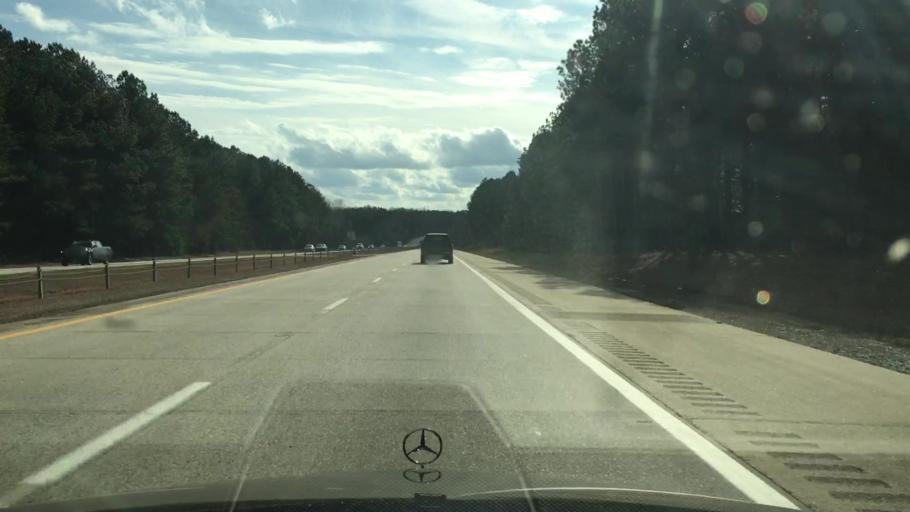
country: US
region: North Carolina
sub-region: Johnston County
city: Clayton
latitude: 35.5700
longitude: -78.5763
